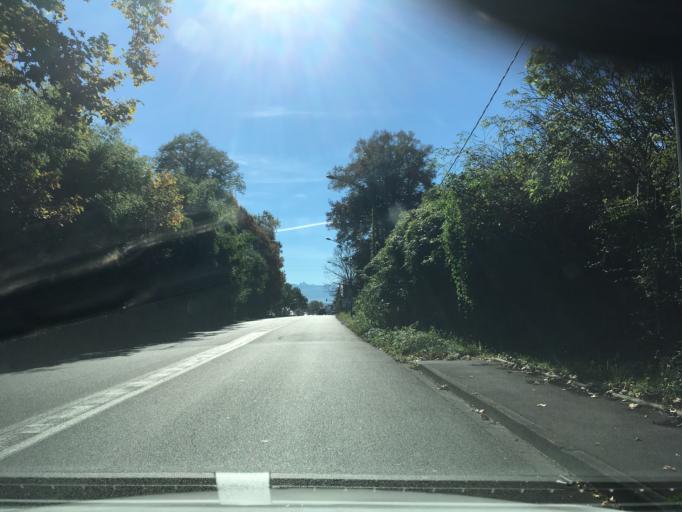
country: FR
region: Aquitaine
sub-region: Departement des Pyrenees-Atlantiques
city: Lons
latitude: 43.3378
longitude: -0.3798
